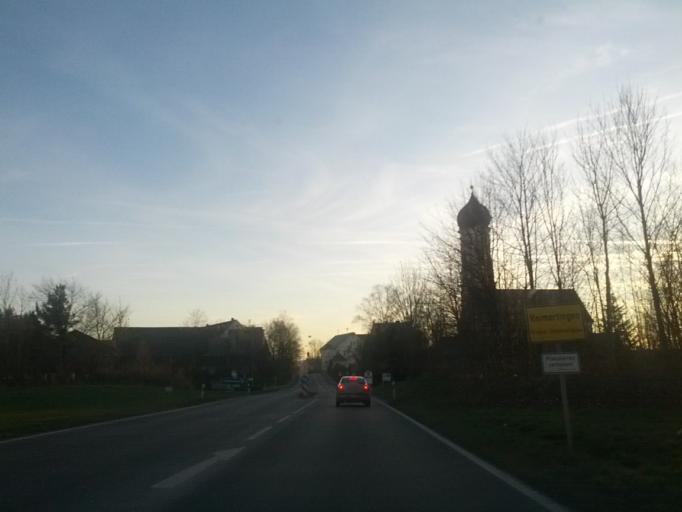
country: DE
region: Bavaria
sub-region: Swabia
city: Heimertingen
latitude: 48.0433
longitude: 10.1543
